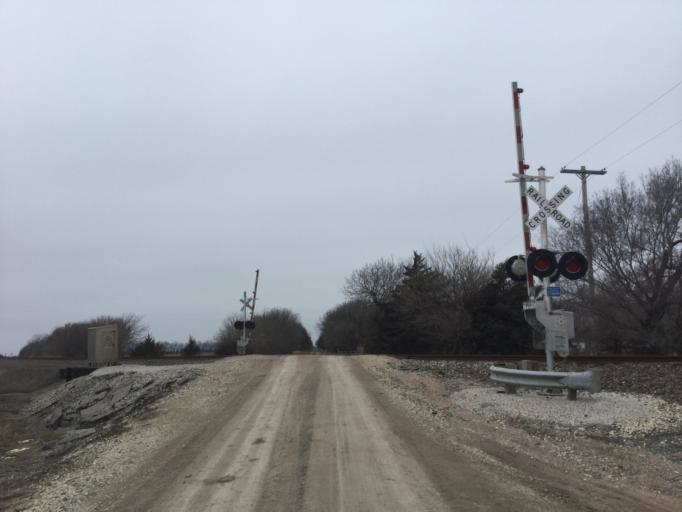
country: US
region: Kansas
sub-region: Butler County
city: Rose Hill
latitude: 37.5337
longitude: -97.1732
